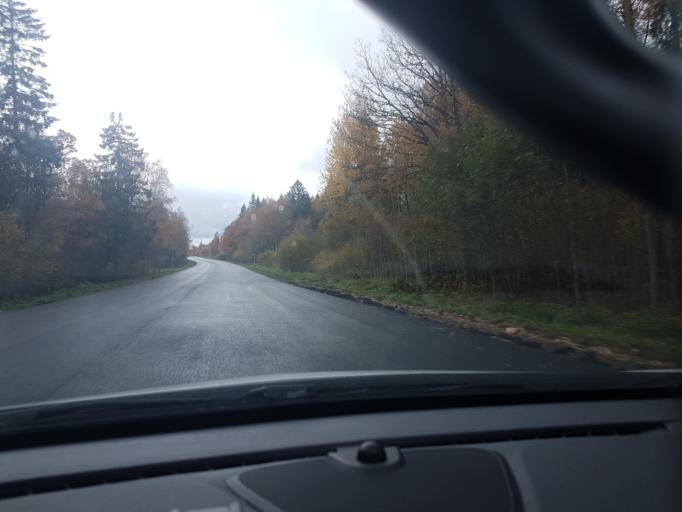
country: RU
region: Moskovskaya
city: Novopetrovskoye
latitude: 55.9999
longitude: 36.3977
